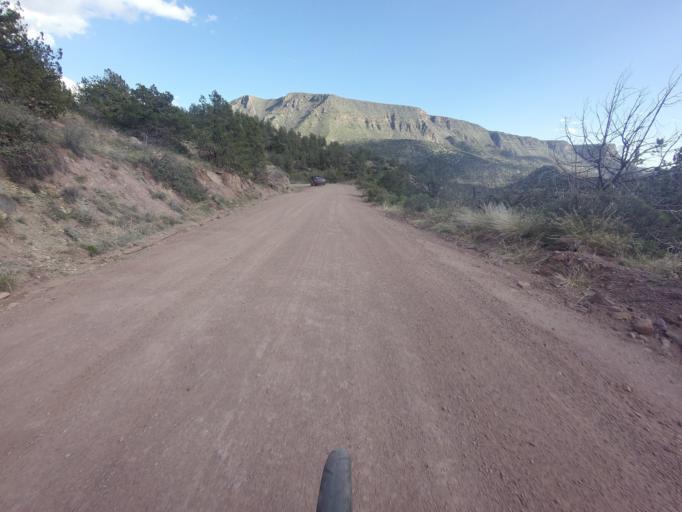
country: US
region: Arizona
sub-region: Gila County
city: Pine
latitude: 34.3985
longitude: -111.6575
